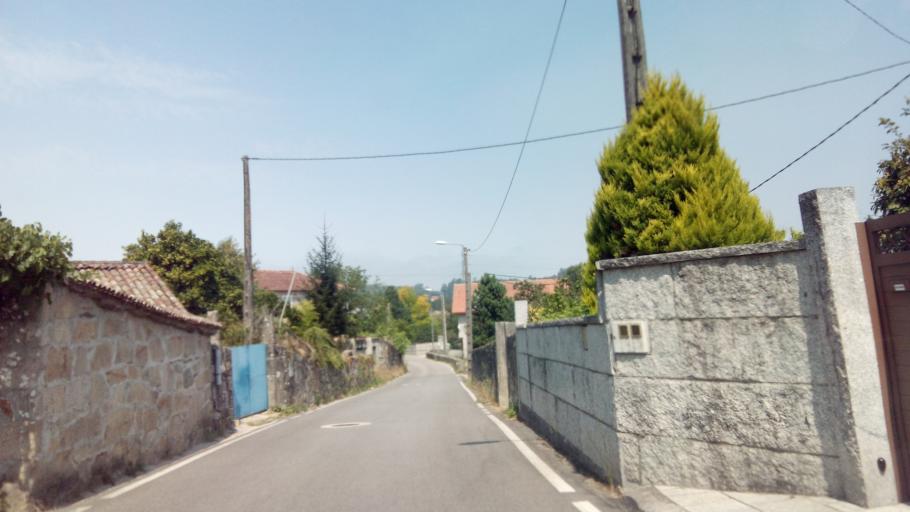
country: ES
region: Galicia
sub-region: Provincia de Pontevedra
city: Nigran
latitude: 42.1101
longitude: -8.7997
